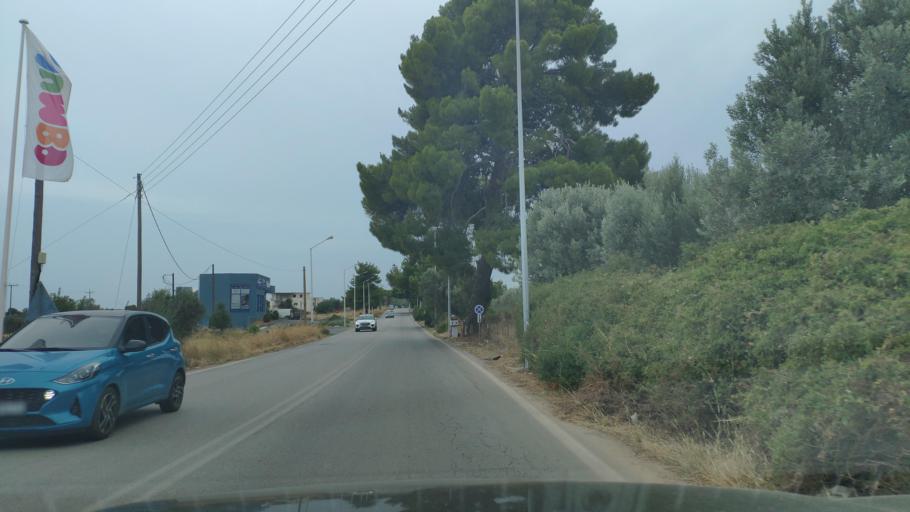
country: GR
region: Peloponnese
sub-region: Nomos Argolidos
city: Porto Cheli
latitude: 37.3422
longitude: 23.1574
